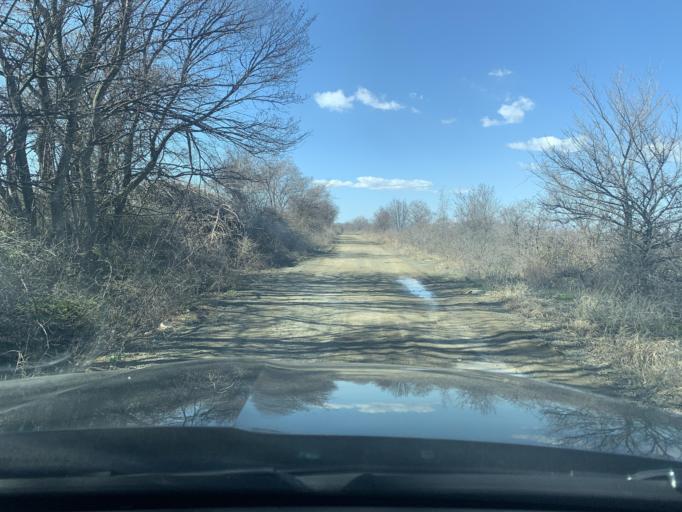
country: MK
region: Demir Kapija
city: Demir Kapija
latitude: 41.4137
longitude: 22.2217
